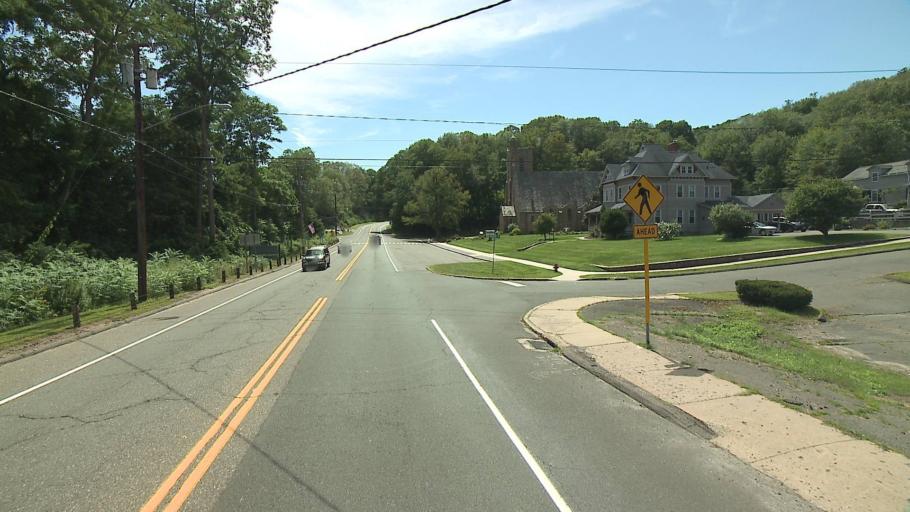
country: US
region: Connecticut
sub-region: Hartford County
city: Collinsville
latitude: 41.8095
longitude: -72.9261
